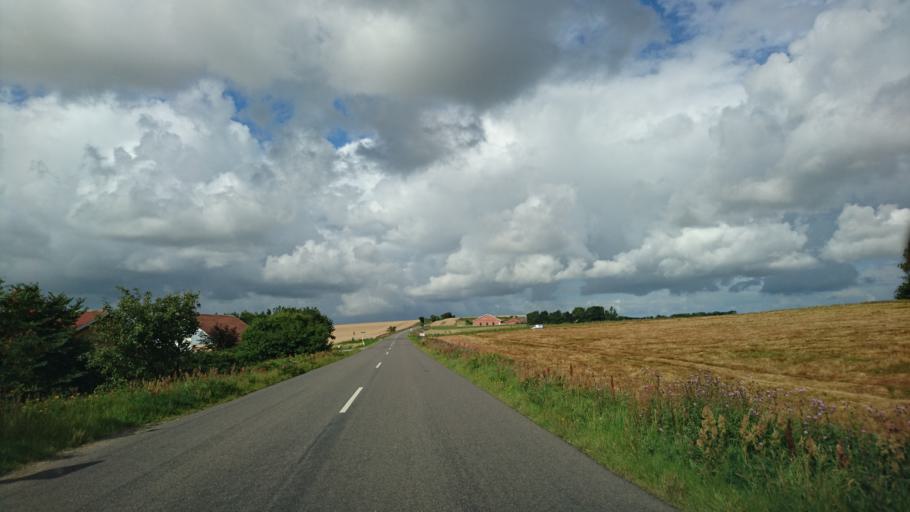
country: DK
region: North Denmark
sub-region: Hjorring Kommune
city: Tars
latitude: 57.3886
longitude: 10.1915
